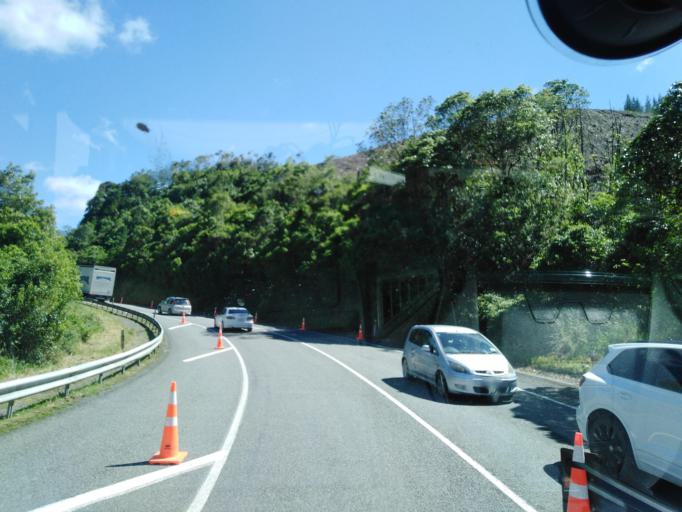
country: NZ
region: Nelson
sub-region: Nelson City
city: Nelson
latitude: -41.2029
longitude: 173.5632
